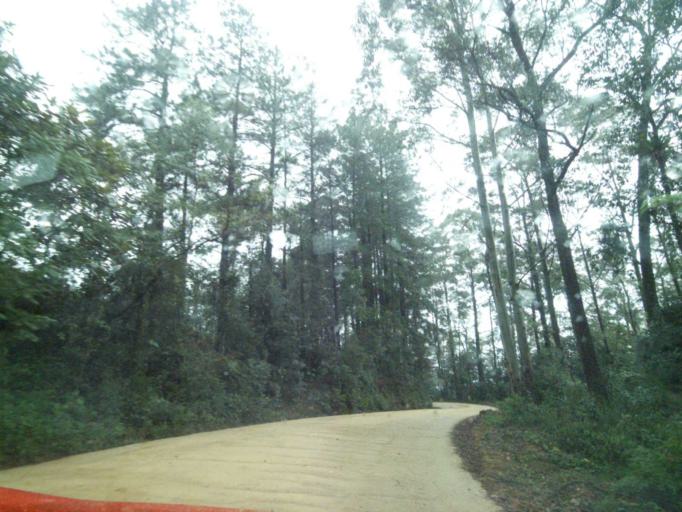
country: BR
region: Santa Catarina
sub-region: Anitapolis
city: Anitapolis
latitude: -27.9257
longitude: -49.1777
